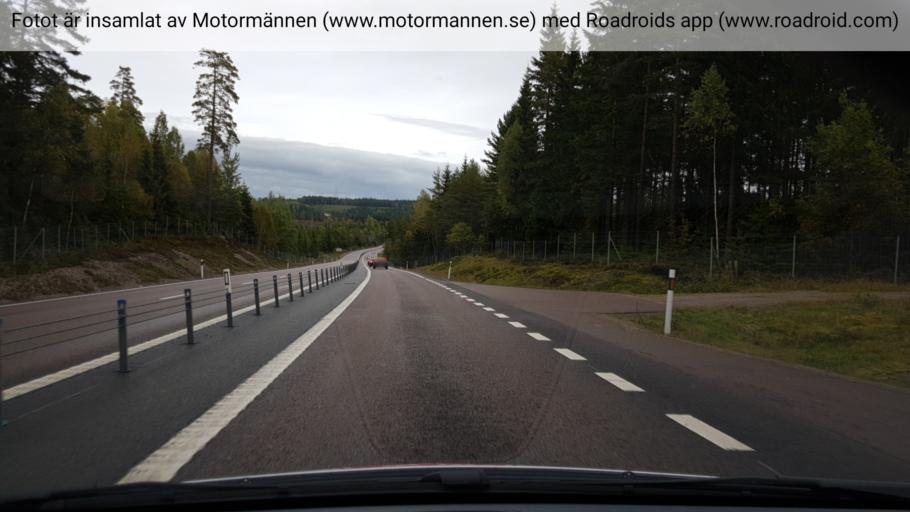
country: SE
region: Vaermland
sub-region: Kristinehamns Kommun
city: Bjorneborg
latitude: 59.3098
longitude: 14.3007
